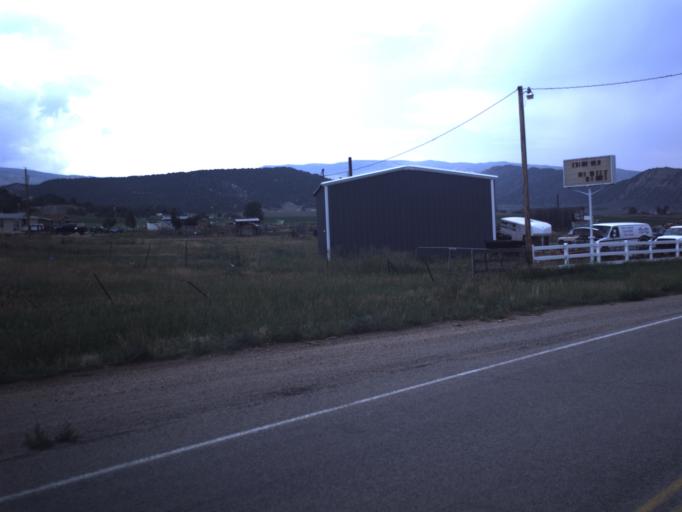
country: US
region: Utah
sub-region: Duchesne County
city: Duchesne
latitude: 40.4036
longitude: -110.7646
